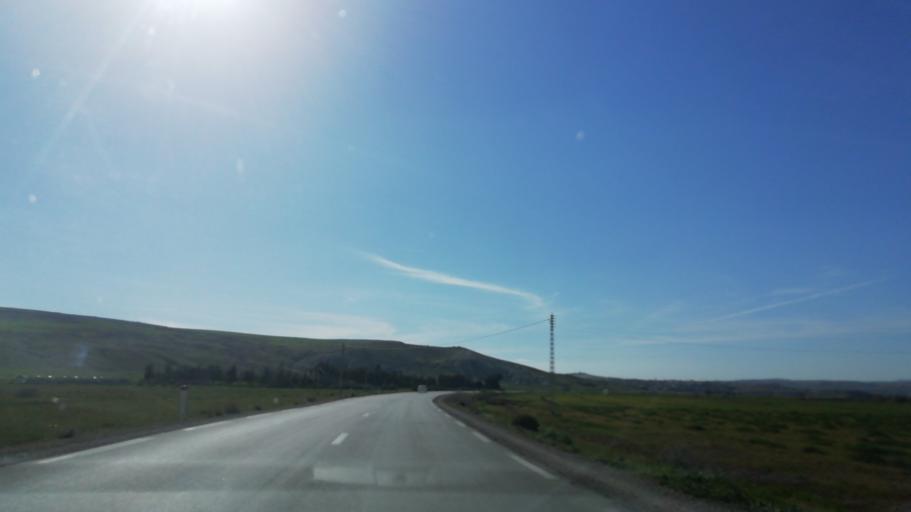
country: DZ
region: Mascara
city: Oued el Abtal
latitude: 35.4565
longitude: 0.7437
